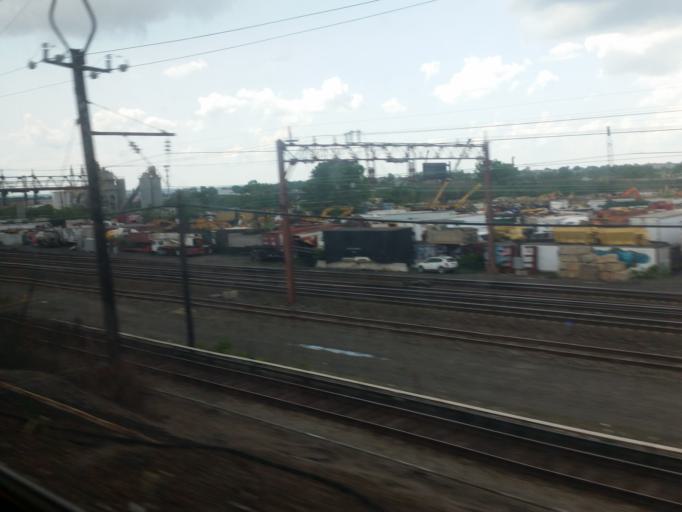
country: US
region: New Jersey
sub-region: Hudson County
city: Harrison
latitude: 40.7430
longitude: -74.1339
